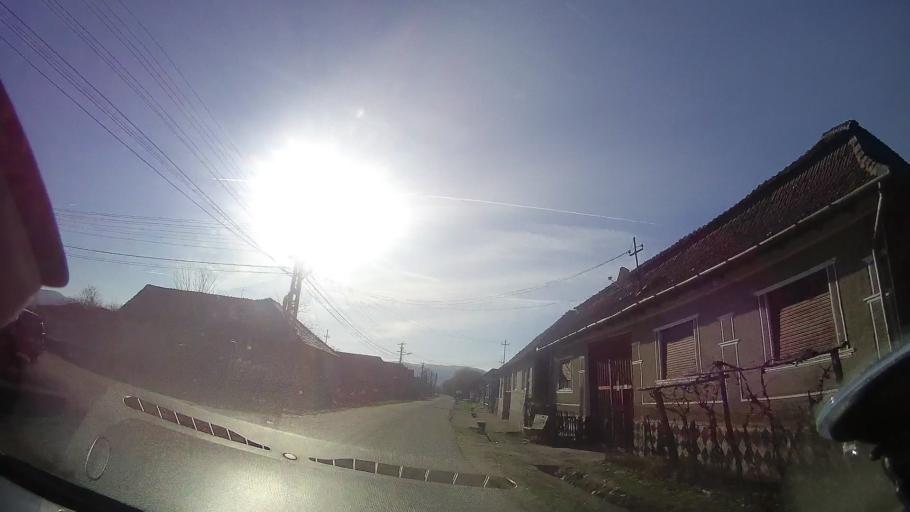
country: RO
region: Bihor
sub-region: Comuna Magesti
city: Magesti
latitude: 47.0222
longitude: 22.4707
